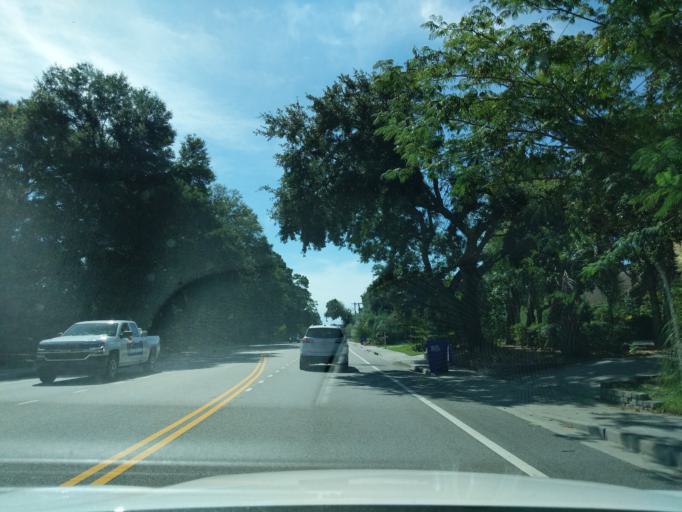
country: US
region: South Carolina
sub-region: Charleston County
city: Charleston
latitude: 32.7463
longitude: -79.9421
